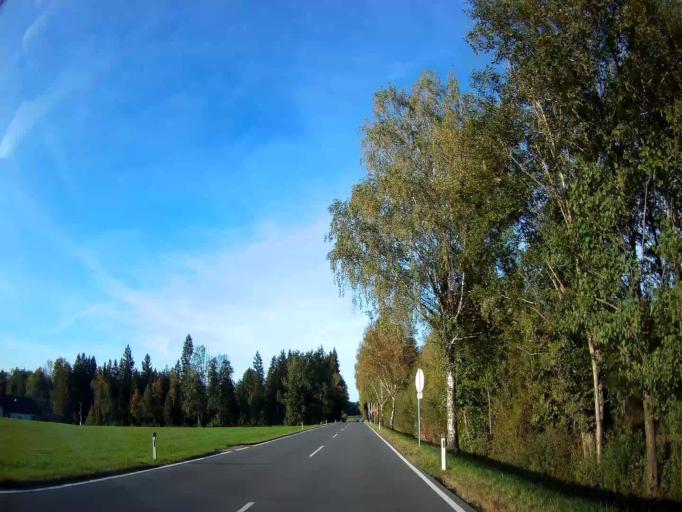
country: DE
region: Bavaria
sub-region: Upper Bavaria
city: Piding
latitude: 47.7558
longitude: 12.9447
